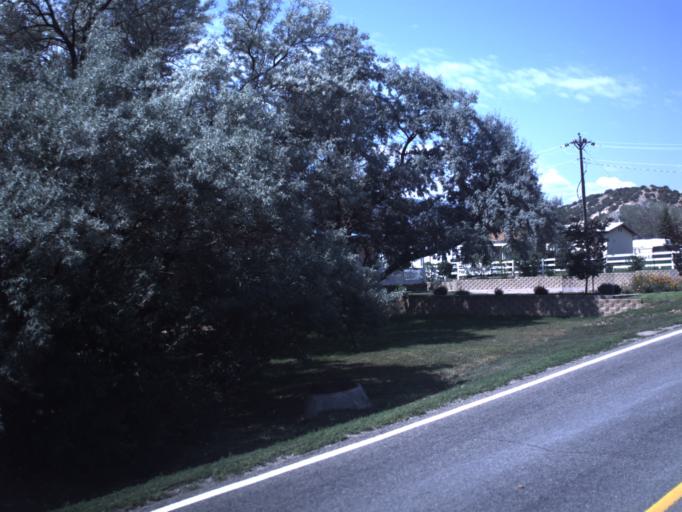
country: US
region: Utah
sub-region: Daggett County
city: Manila
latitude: 40.9882
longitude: -109.7294
